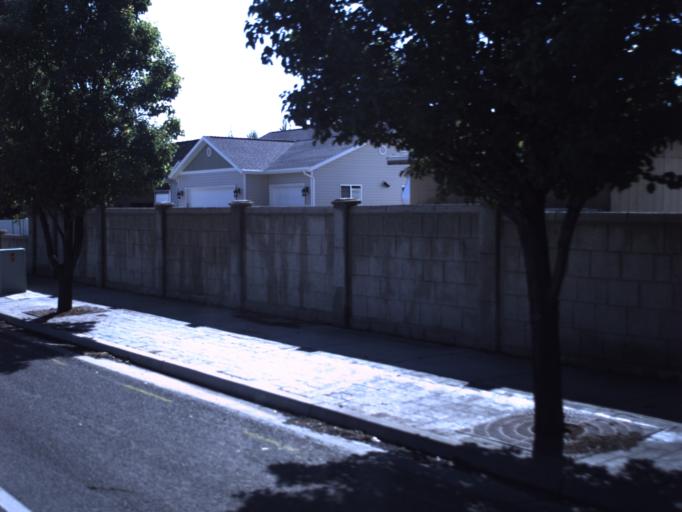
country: US
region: Utah
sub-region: Utah County
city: Spanish Fork
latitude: 40.1080
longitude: -111.6703
